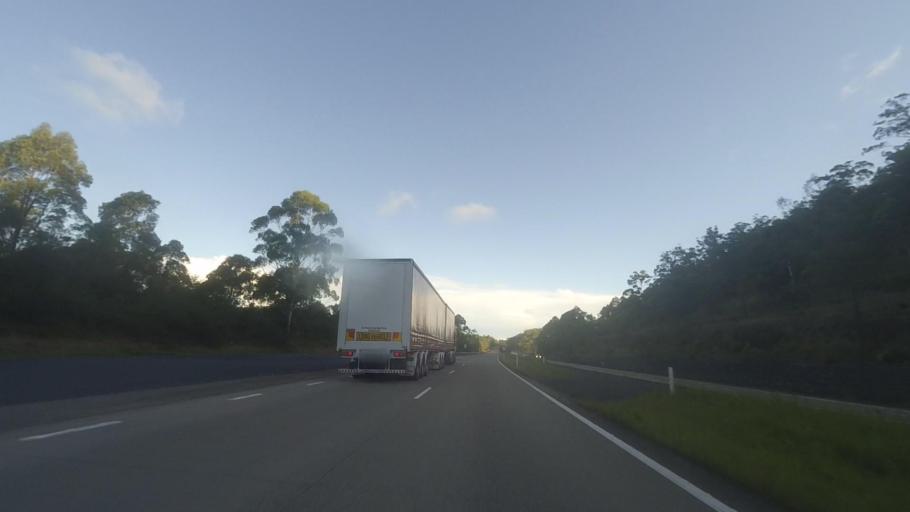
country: AU
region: New South Wales
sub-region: Great Lakes
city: Bulahdelah
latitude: -32.2876
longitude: 152.3411
